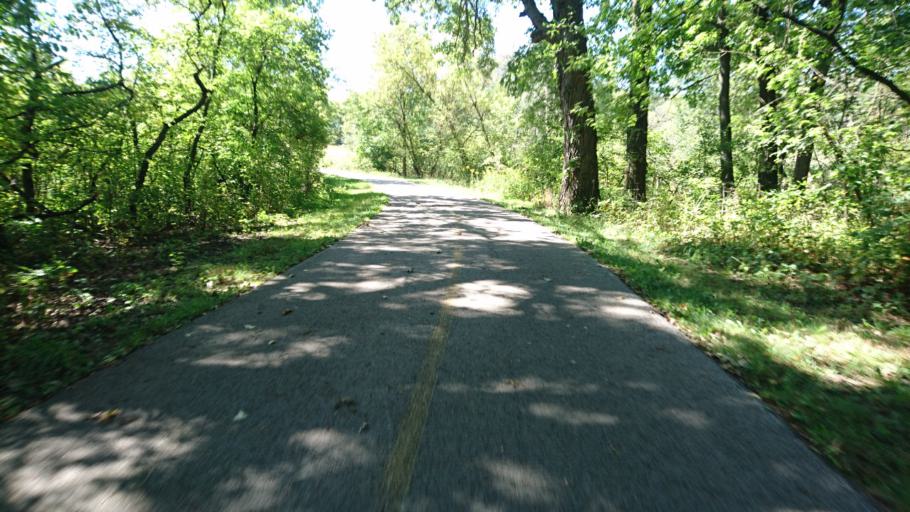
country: US
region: Illinois
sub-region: Cook County
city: Lansing
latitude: 41.5567
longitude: -87.5538
